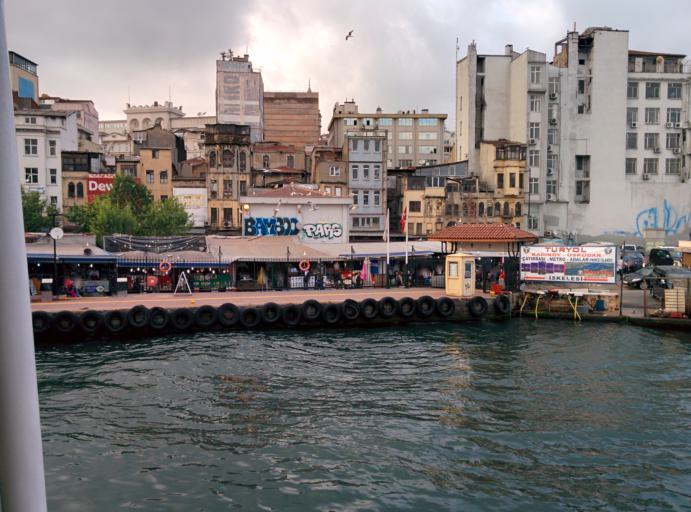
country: TR
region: Istanbul
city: Eminoenue
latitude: 41.0215
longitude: 28.9737
